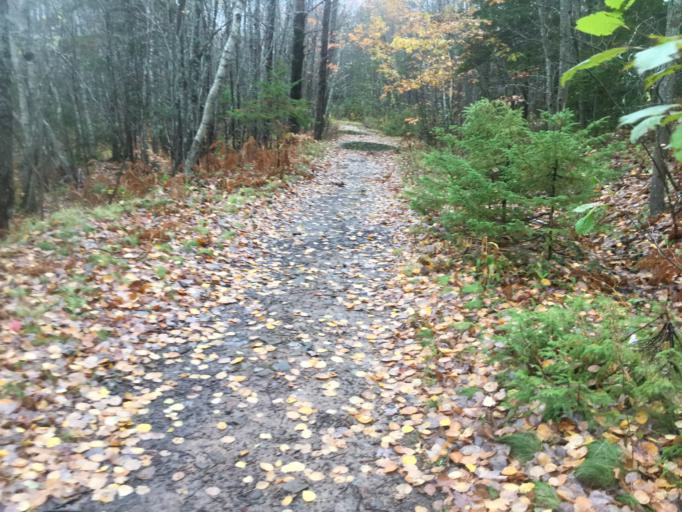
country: CA
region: Nova Scotia
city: New Glasgow
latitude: 45.5503
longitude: -62.6788
